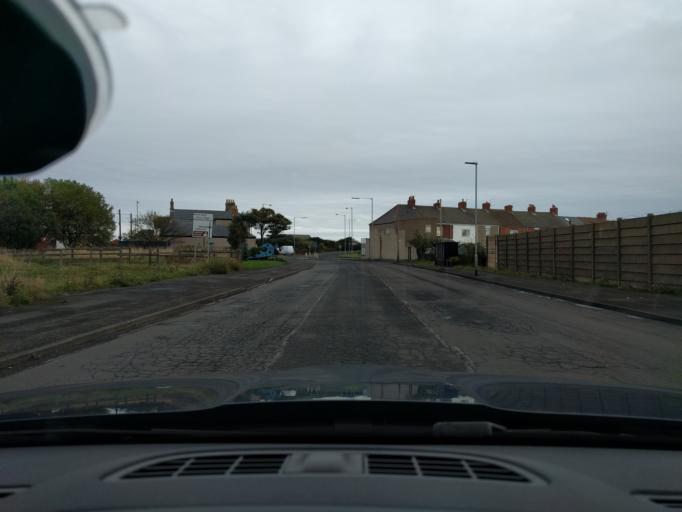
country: GB
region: England
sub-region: Northumberland
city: Blyth
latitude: 55.1439
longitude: -1.5216
